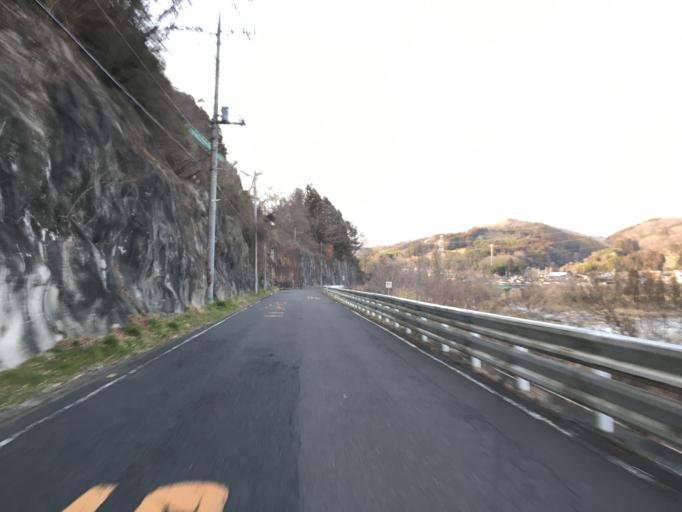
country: JP
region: Ibaraki
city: Daigo
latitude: 36.8113
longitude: 140.3700
